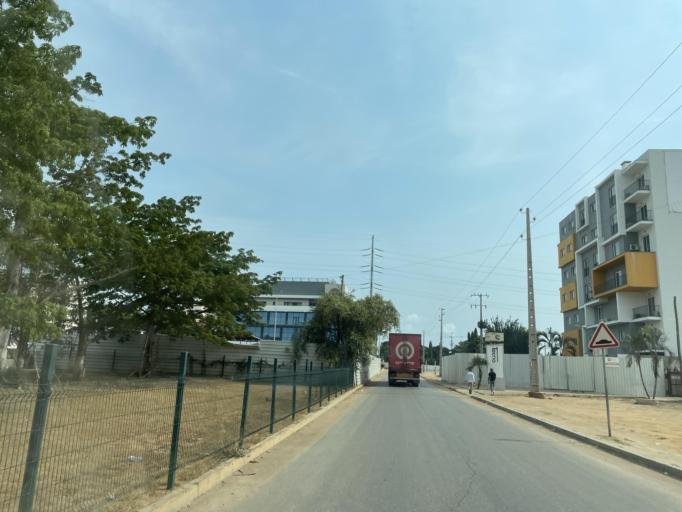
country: AO
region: Luanda
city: Luanda
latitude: -8.9058
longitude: 13.1975
